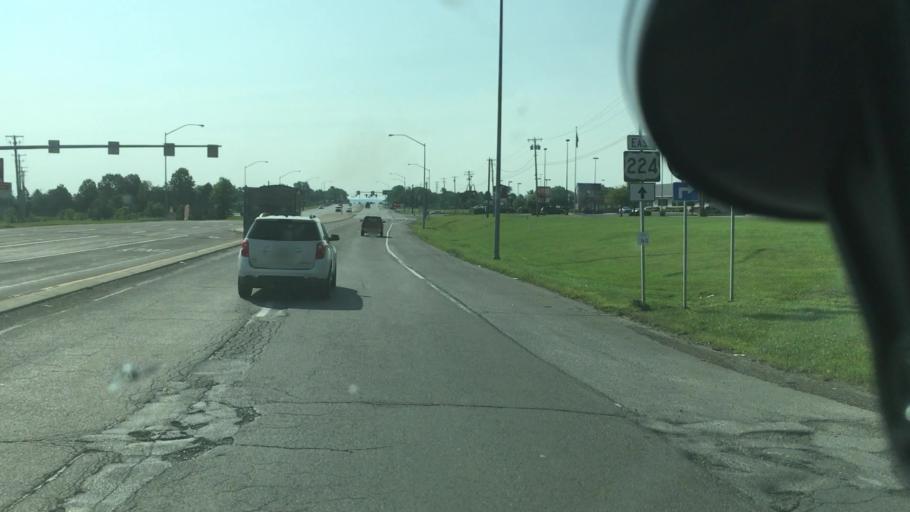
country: US
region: Pennsylvania
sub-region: Lawrence County
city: Oakwood
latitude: 41.0131
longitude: -80.3971
